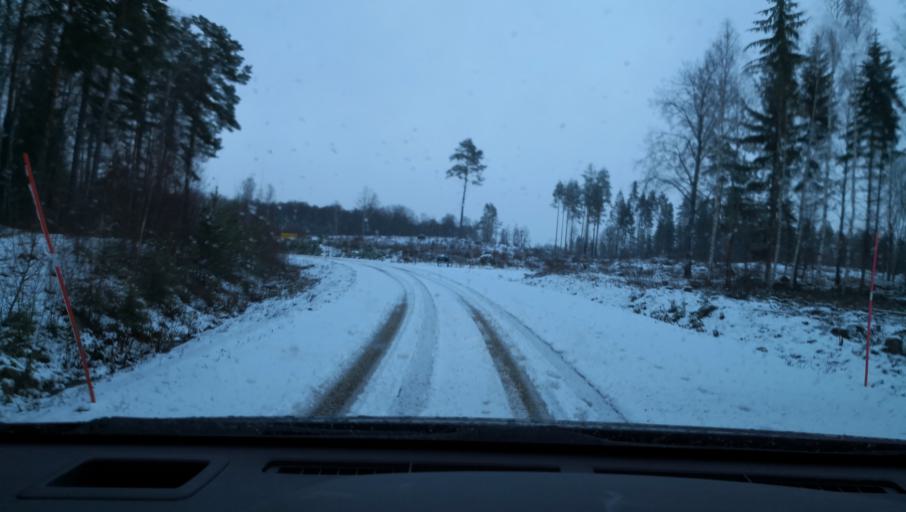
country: SE
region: Vaestmanland
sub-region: Kopings Kommun
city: Koping
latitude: 59.4774
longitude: 15.9623
